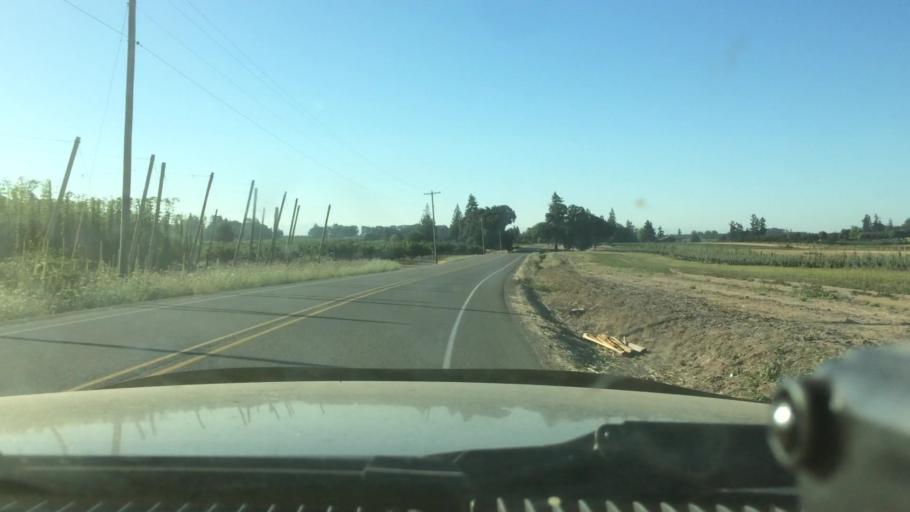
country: US
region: Oregon
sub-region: Marion County
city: Gervais
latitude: 45.1255
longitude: -122.9895
